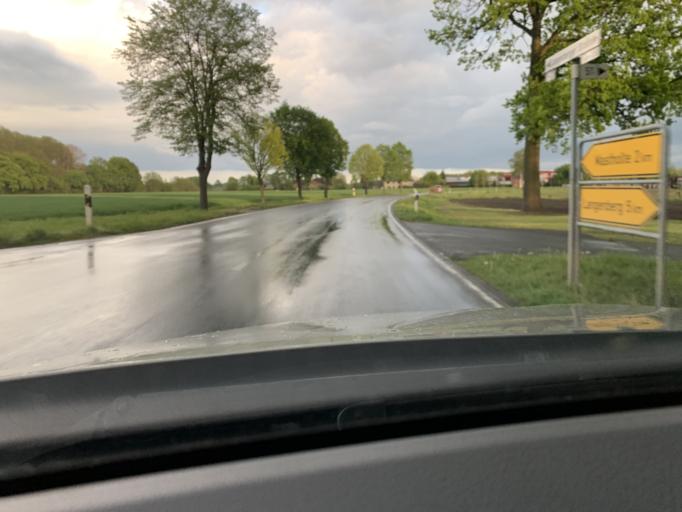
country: DE
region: North Rhine-Westphalia
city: Rietberg
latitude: 51.7714
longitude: 8.3841
